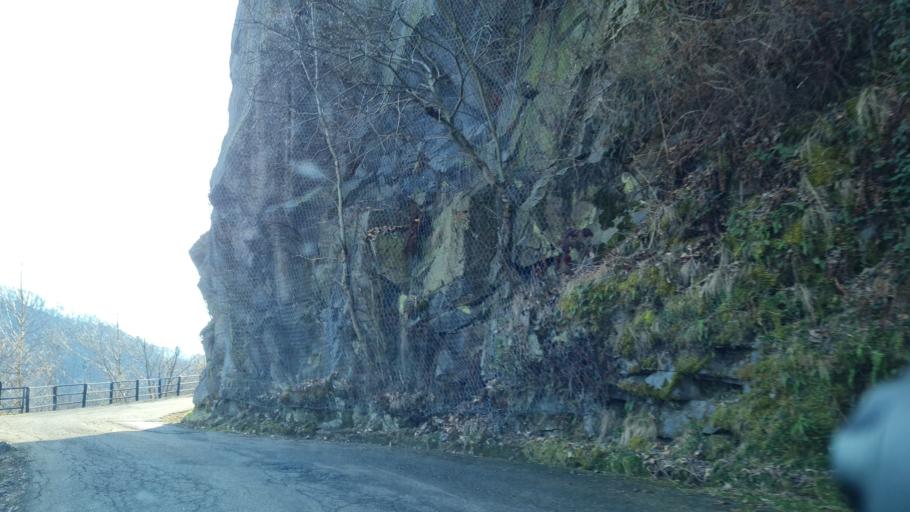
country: IT
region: Piedmont
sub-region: Provincia di Biella
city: San Paolo Cervo
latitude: 45.6438
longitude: 8.0189
